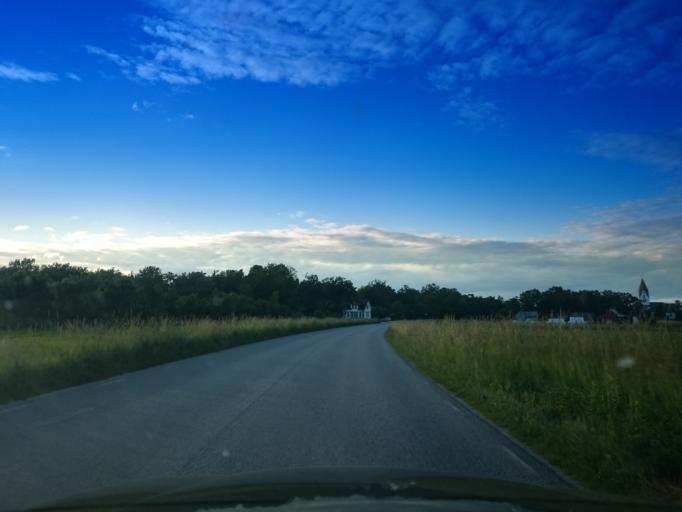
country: SE
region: Gotland
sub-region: Gotland
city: Hemse
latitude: 57.3077
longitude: 18.3800
